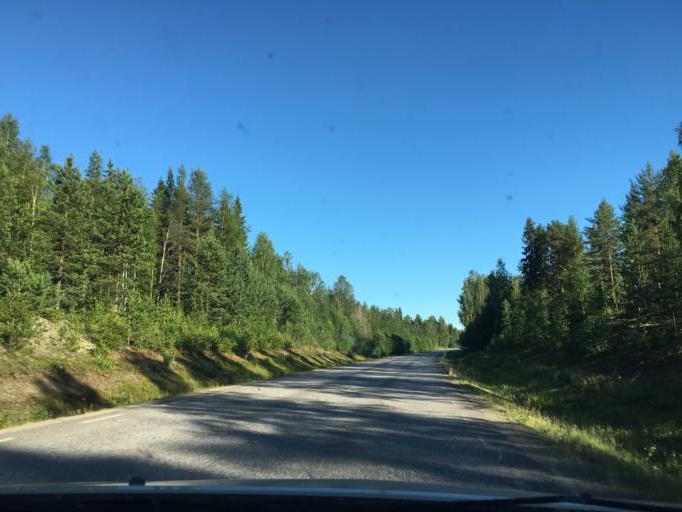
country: SE
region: Norrbotten
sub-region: Kalix Kommun
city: Rolfs
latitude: 65.9142
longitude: 22.9247
